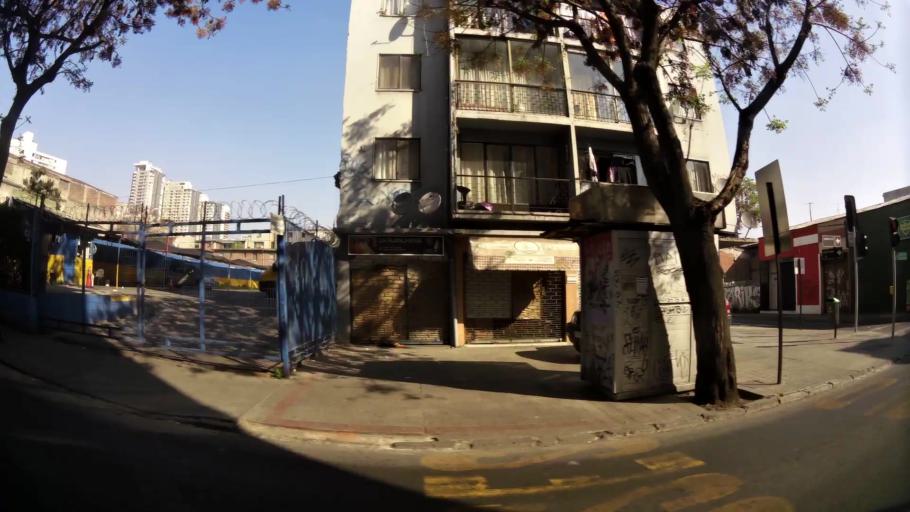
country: CL
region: Santiago Metropolitan
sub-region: Provincia de Santiago
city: Santiago
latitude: -33.4396
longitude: -70.6621
